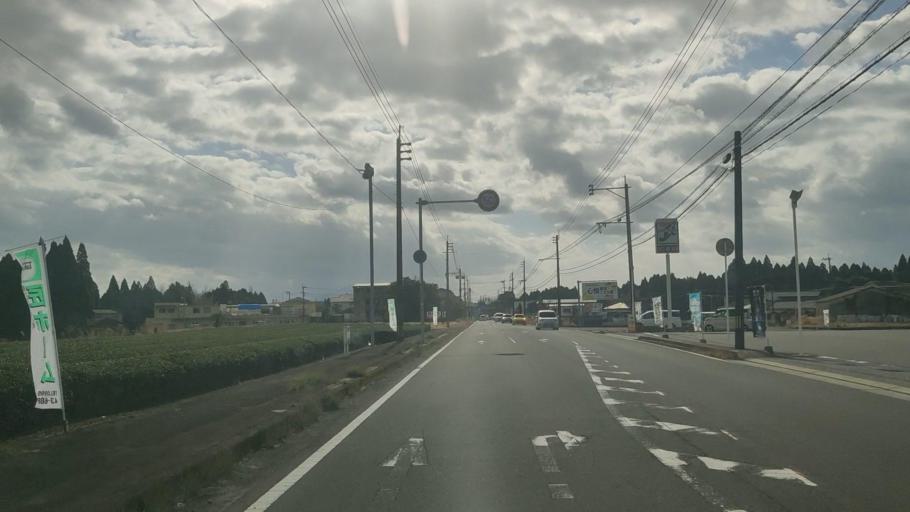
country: JP
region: Kagoshima
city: Kajiki
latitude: 31.7814
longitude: 130.7043
